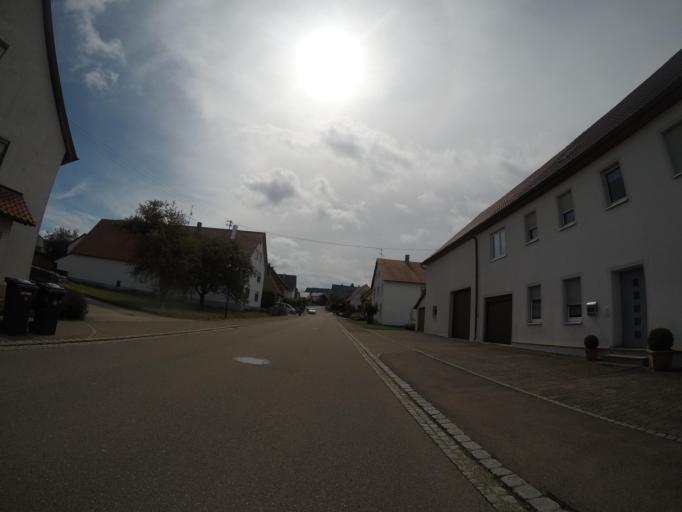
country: DE
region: Baden-Wuerttemberg
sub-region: Tuebingen Region
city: Laichingen
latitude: 48.4483
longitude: 9.6677
